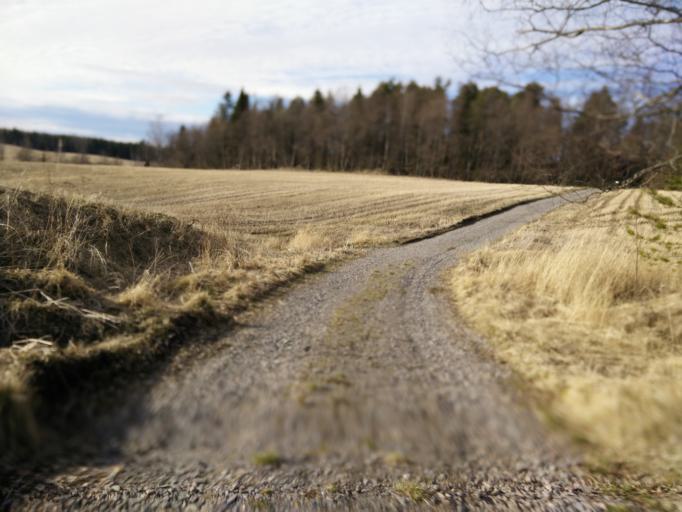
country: FI
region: Pirkanmaa
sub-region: Tampere
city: Orivesi
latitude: 61.7098
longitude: 24.3207
